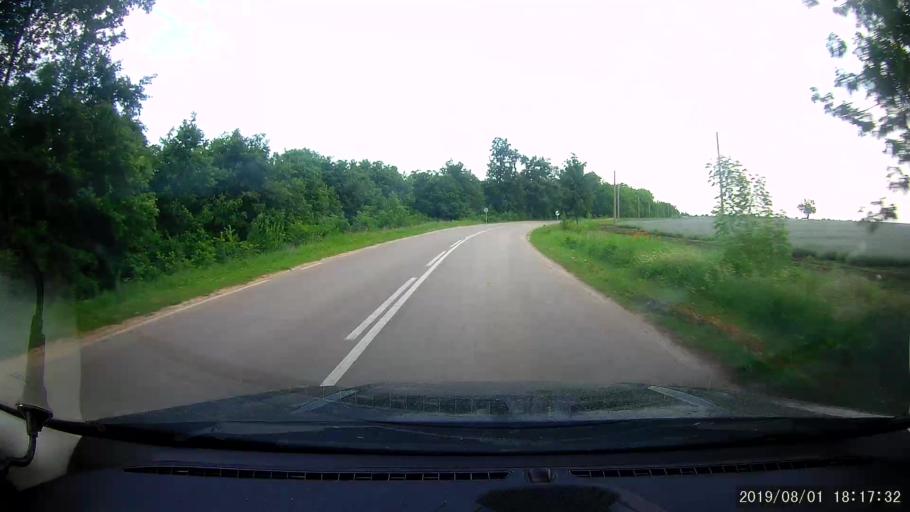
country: BG
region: Shumen
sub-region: Obshtina Kaolinovo
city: Kaolinovo
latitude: 43.7121
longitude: 27.0828
